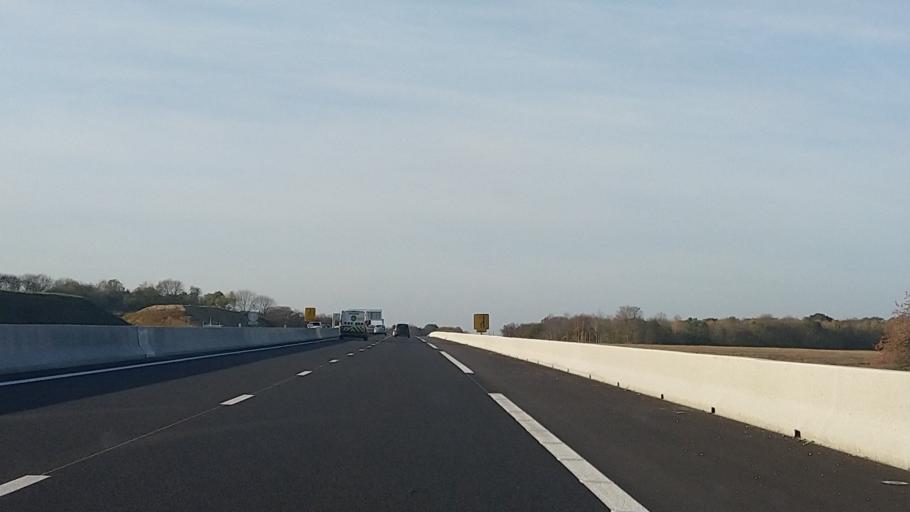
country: FR
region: Ile-de-France
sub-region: Departement du Val-d'Oise
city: Maffliers
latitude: 49.0871
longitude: 2.3154
